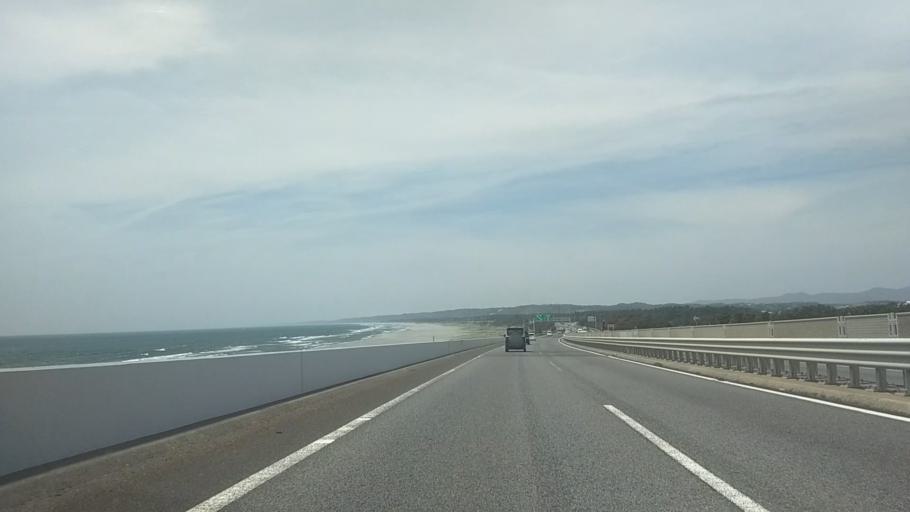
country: JP
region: Shizuoka
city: Kosai-shi
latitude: 34.6792
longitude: 137.5918
